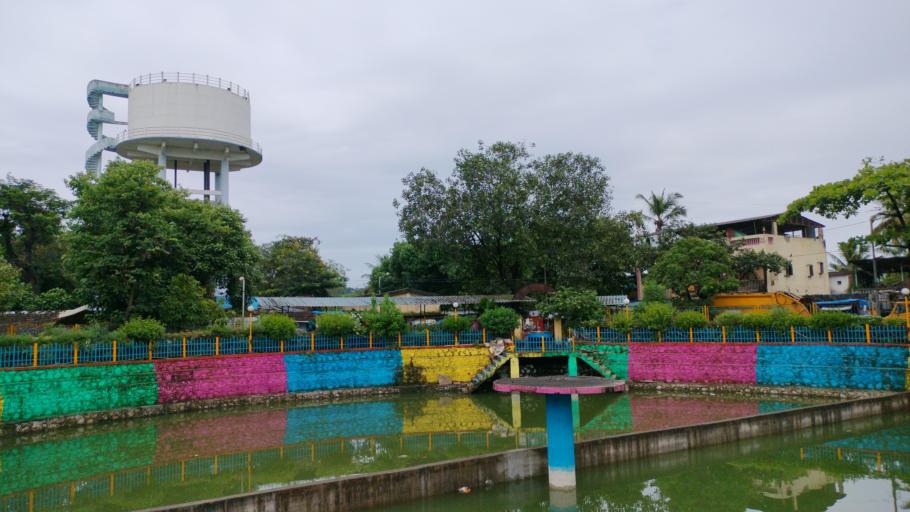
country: IN
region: Maharashtra
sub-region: Thane
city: Bhayandar
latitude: 19.2913
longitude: 72.8145
